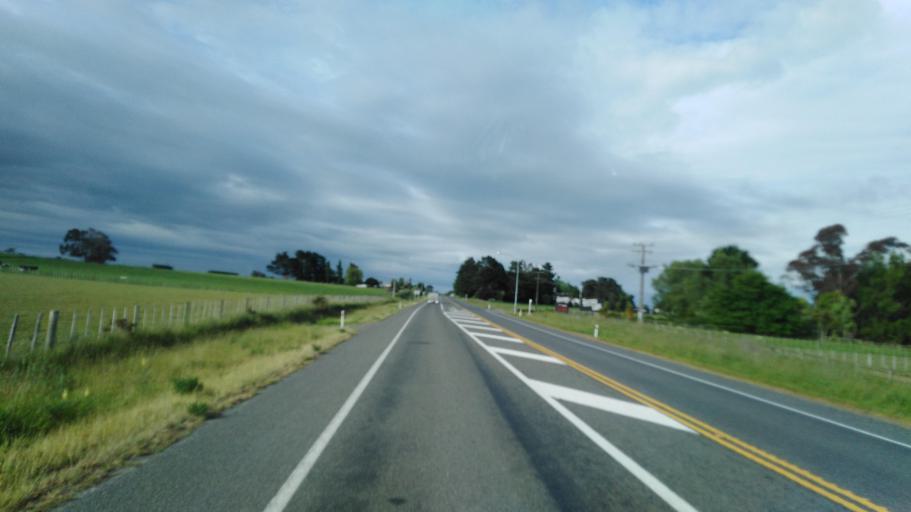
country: NZ
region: Manawatu-Wanganui
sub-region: Rangitikei District
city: Bulls
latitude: -40.2288
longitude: 175.4161
